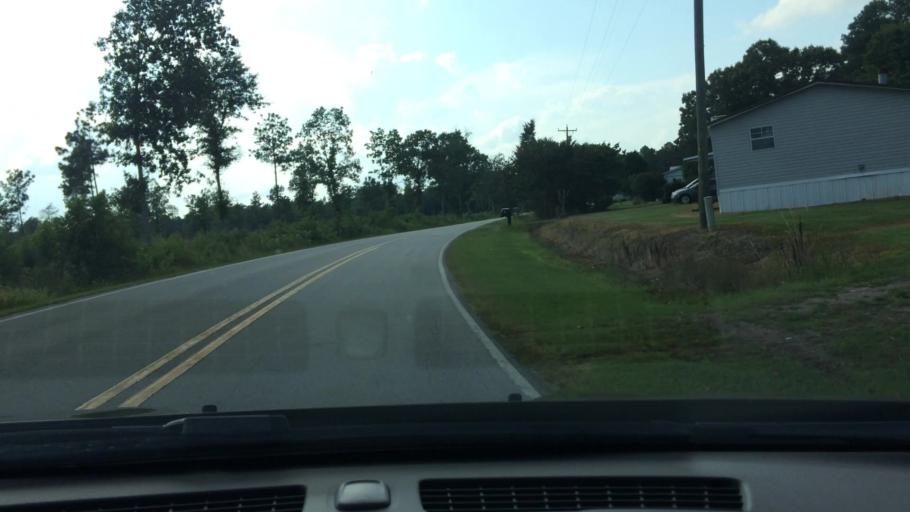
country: US
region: North Carolina
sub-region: Beaufort County
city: River Road
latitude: 35.4316
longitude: -76.9806
